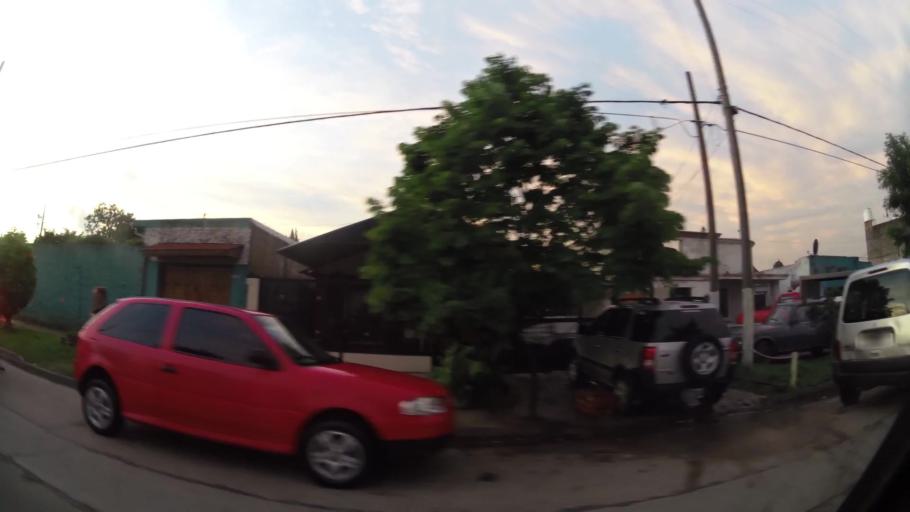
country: AR
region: Buenos Aires
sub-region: Partido de Lomas de Zamora
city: Lomas de Zamora
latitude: -34.7541
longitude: -58.3610
